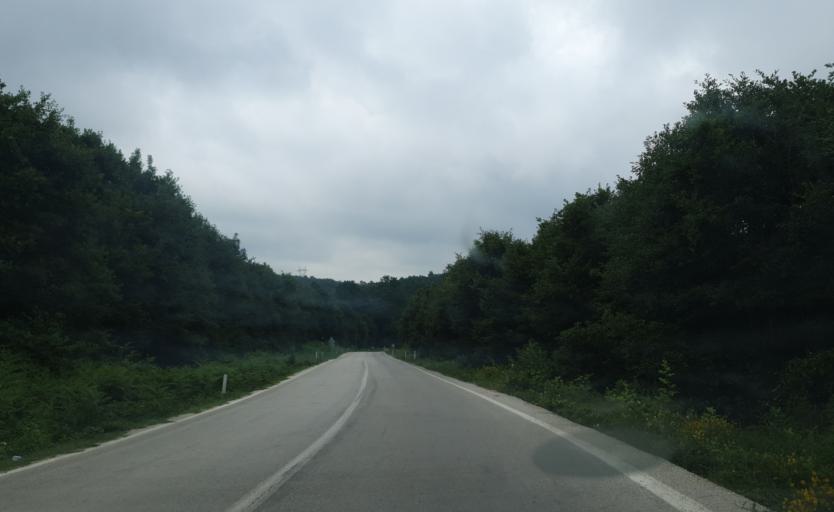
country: TR
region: Kirklareli
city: Salmydessus
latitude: 41.5831
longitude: 28.0713
